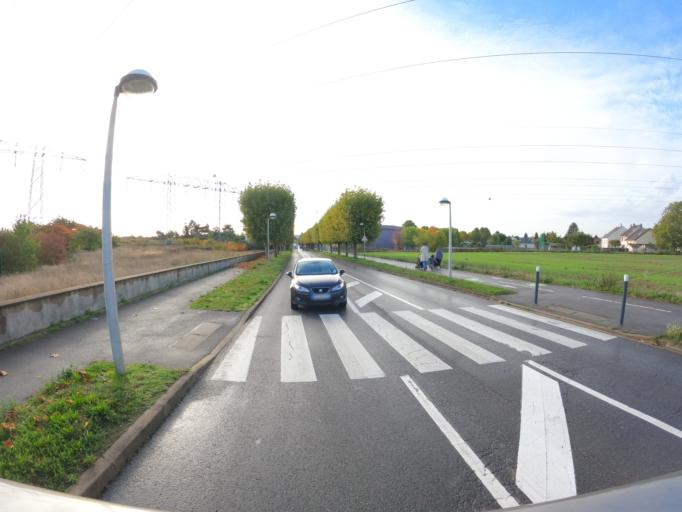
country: FR
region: Ile-de-France
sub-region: Departement de Seine-et-Marne
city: Brou-sur-Chantereine
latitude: 48.8893
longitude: 2.6200
